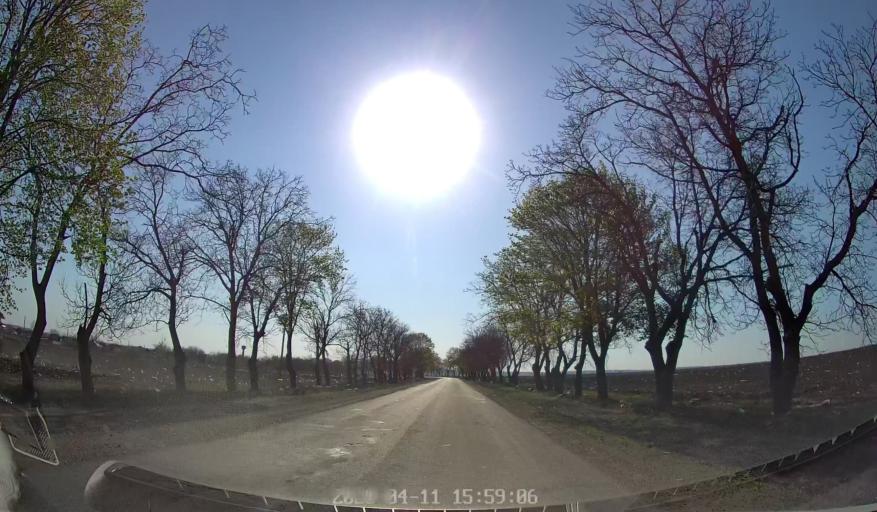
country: MD
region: Chisinau
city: Vadul lui Voda
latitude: 47.0833
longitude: 29.1459
